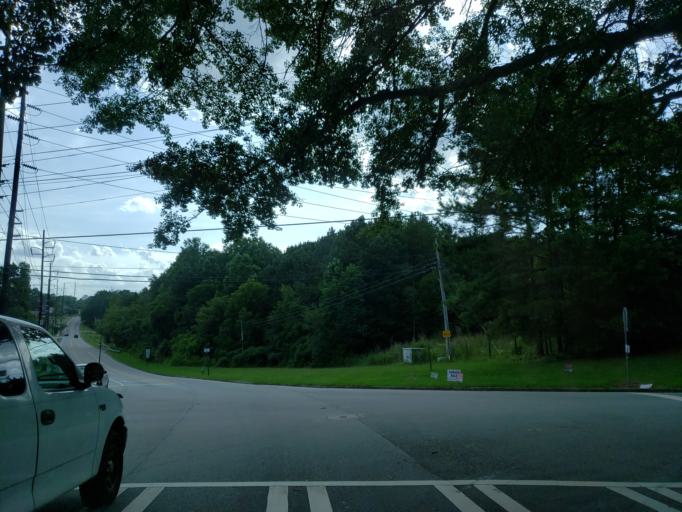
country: US
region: Georgia
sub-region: Cobb County
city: Powder Springs
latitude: 33.8768
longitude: -84.6586
